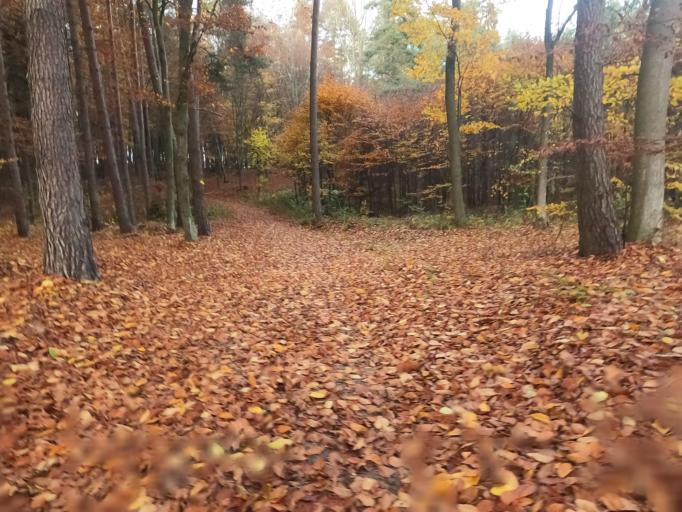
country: PL
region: Pomeranian Voivodeship
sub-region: Powiat starogardzki
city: Skarszewy
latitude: 54.0150
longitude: 18.4624
